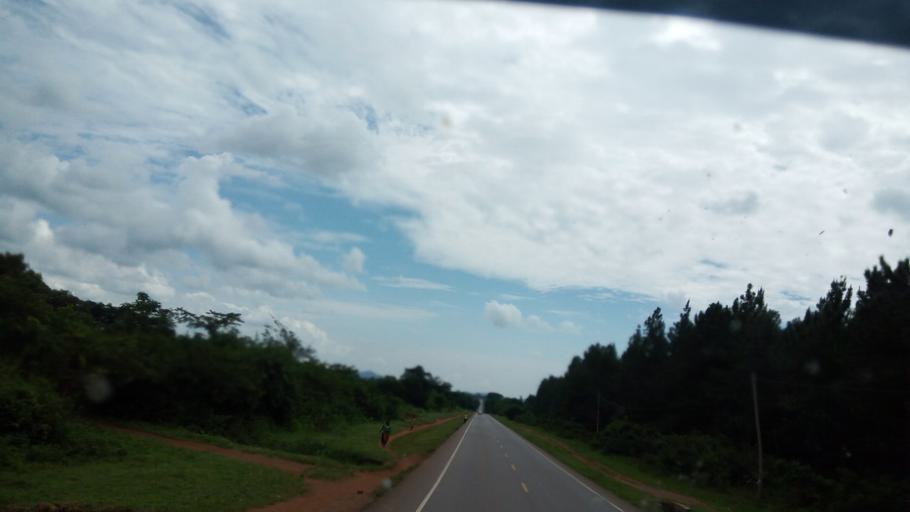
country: UG
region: Central Region
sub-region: Nakasongola District
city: Nakasongola
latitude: 1.1951
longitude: 32.4620
